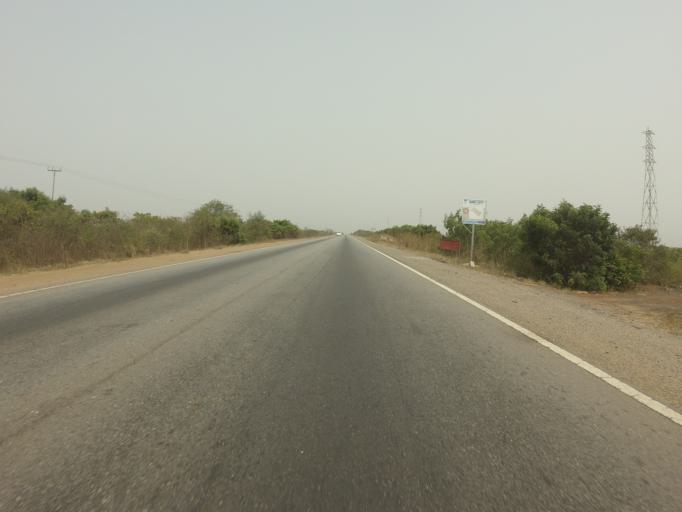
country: GH
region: Greater Accra
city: Tema
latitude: 5.7994
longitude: 0.1358
